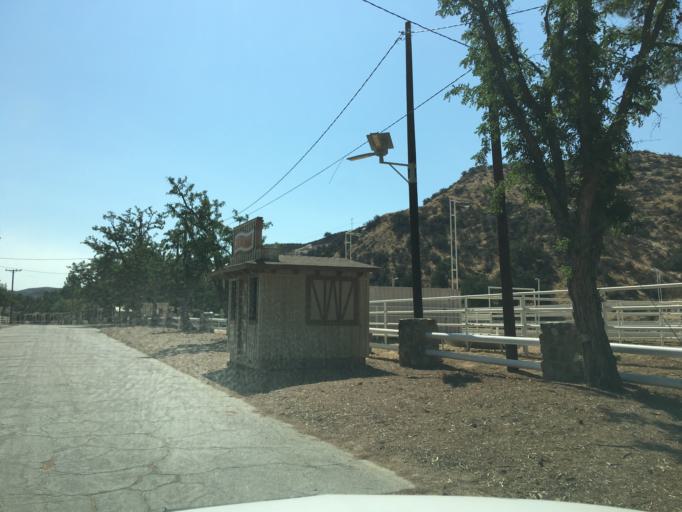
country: US
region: California
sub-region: Los Angeles County
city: Castaic
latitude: 34.4790
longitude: -118.6080
